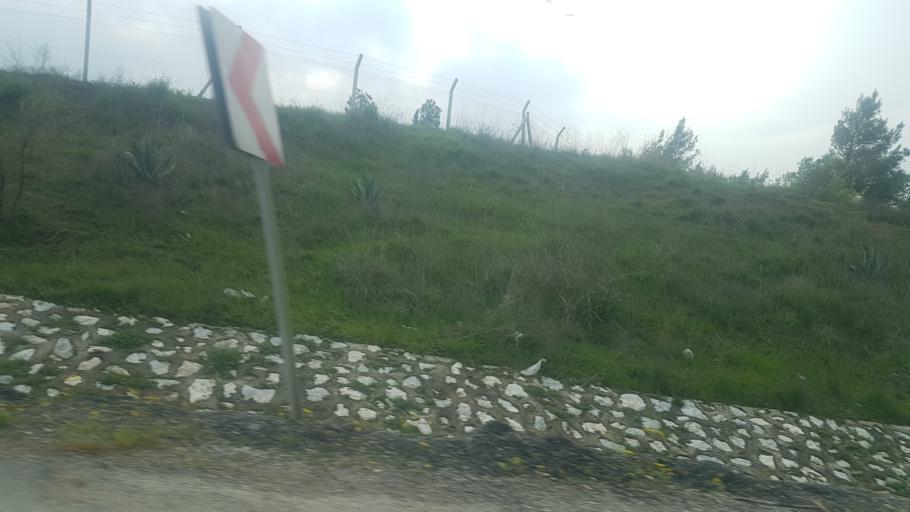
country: TR
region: Mersin
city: Yenice
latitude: 37.0744
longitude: 35.1686
